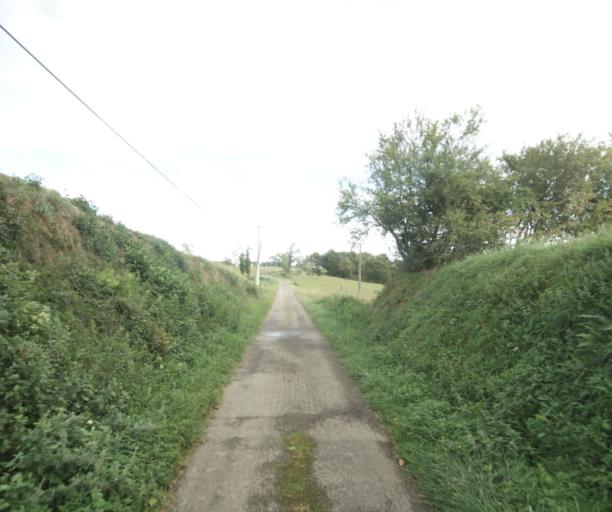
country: FR
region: Midi-Pyrenees
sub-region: Departement du Gers
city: Cazaubon
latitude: 43.8870
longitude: -0.1407
